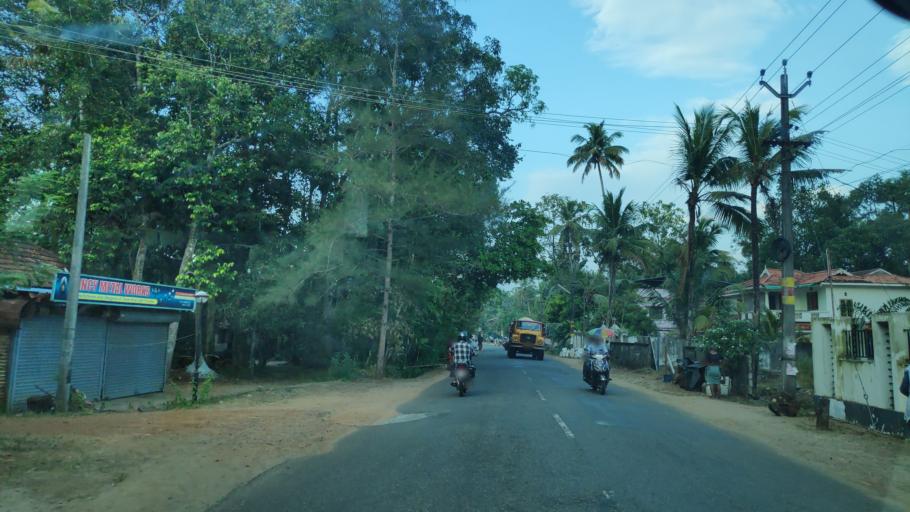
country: IN
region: Kerala
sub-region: Alappuzha
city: Shertallai
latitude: 9.6454
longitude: 76.3707
